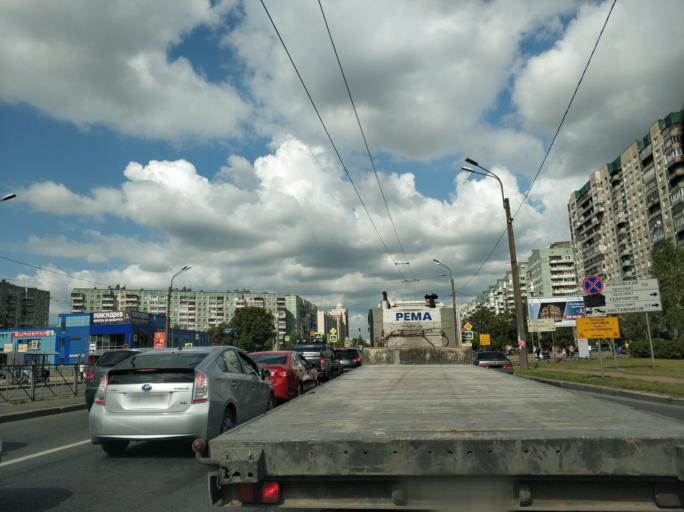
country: RU
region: St.-Petersburg
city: Krasnogvargeisky
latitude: 59.9507
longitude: 30.4725
